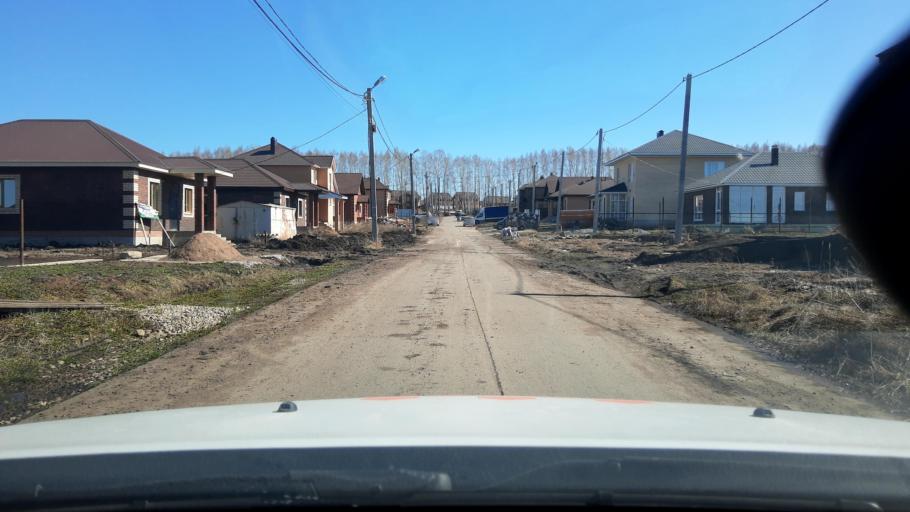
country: RU
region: Bashkortostan
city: Kabakovo
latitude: 54.6162
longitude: 56.1143
